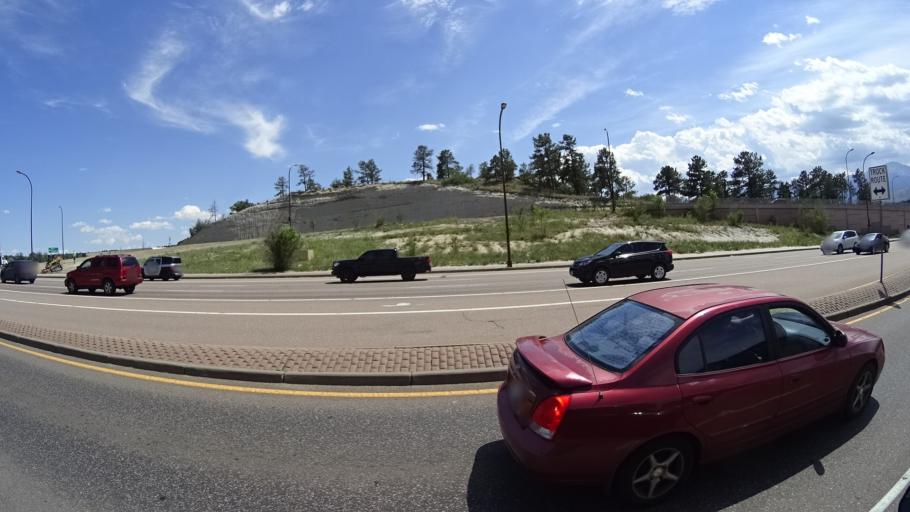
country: US
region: Colorado
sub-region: El Paso County
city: Air Force Academy
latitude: 38.9331
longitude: -104.8090
